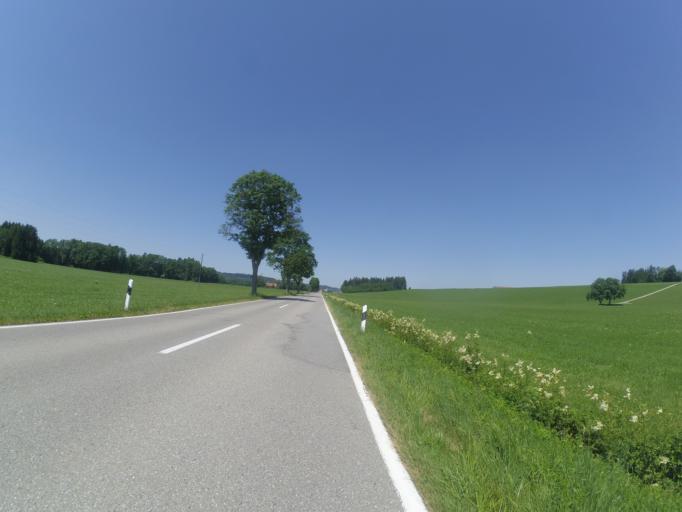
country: DE
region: Bavaria
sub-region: Swabia
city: Bohen
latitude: 47.9015
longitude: 10.3171
